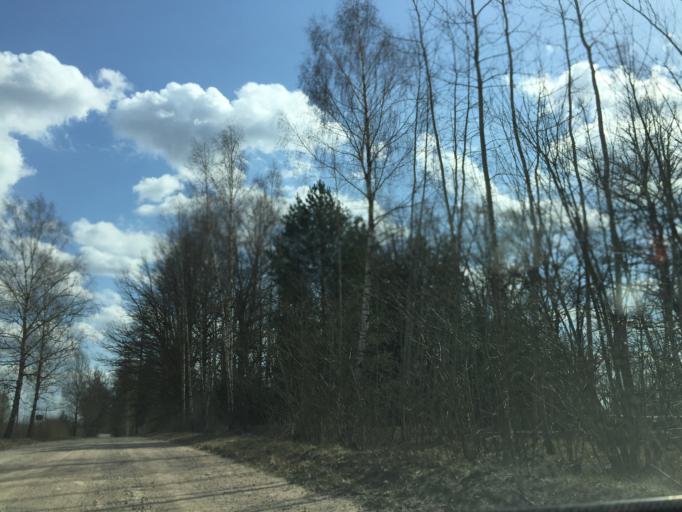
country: LV
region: Skriveri
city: Skriveri
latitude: 56.7533
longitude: 25.0784
